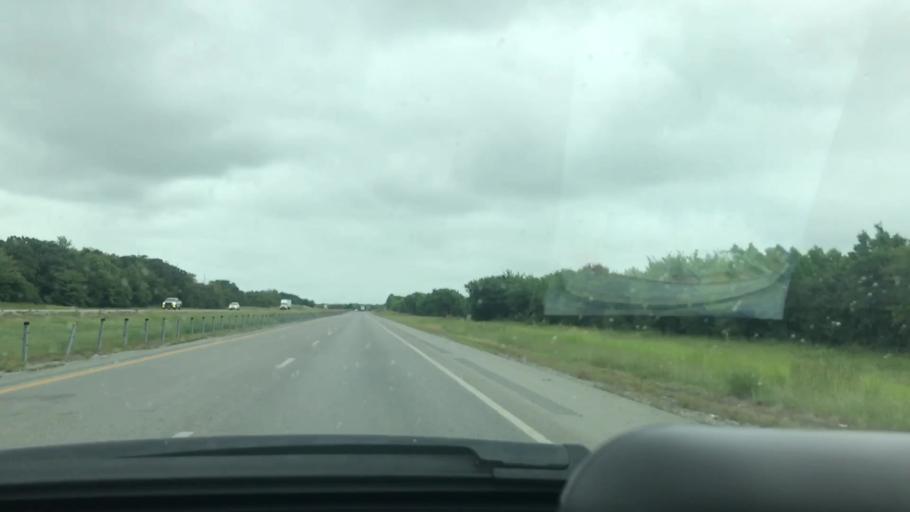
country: US
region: Oklahoma
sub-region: Coal County
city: Coalgate
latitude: 34.6381
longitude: -95.9512
